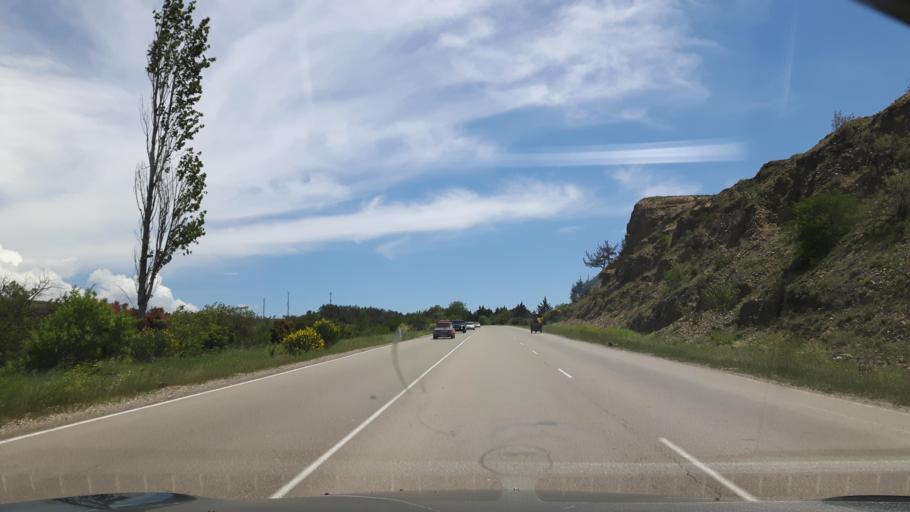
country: GE
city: Didi Lilo
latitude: 41.6926
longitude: 45.0754
